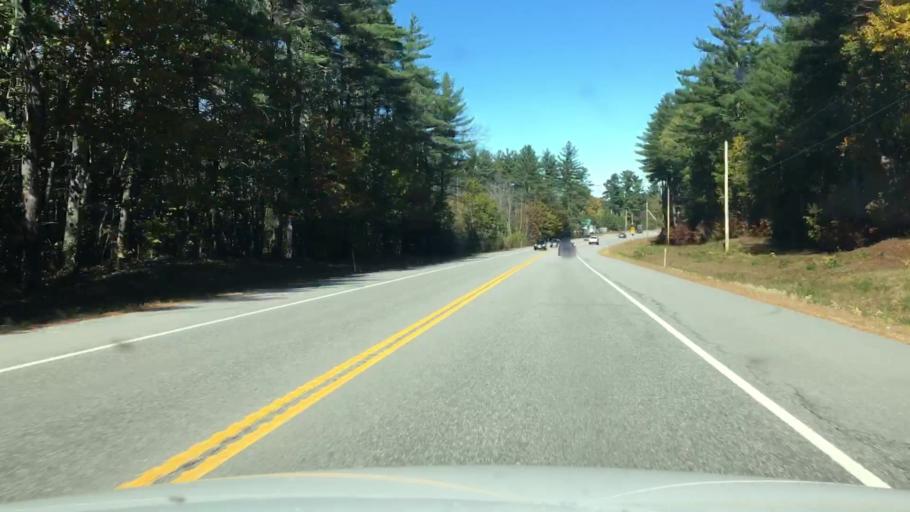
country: US
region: New Hampshire
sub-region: Carroll County
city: Ossipee
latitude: 43.6654
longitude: -71.0718
